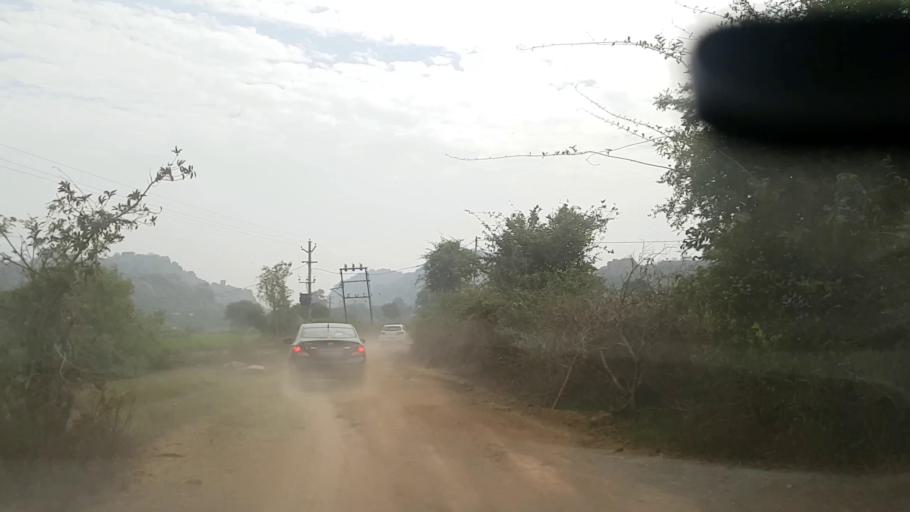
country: IN
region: Telangana
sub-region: Rangareddi
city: Lal Bahadur Nagar
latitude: 17.1810
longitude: 78.7885
